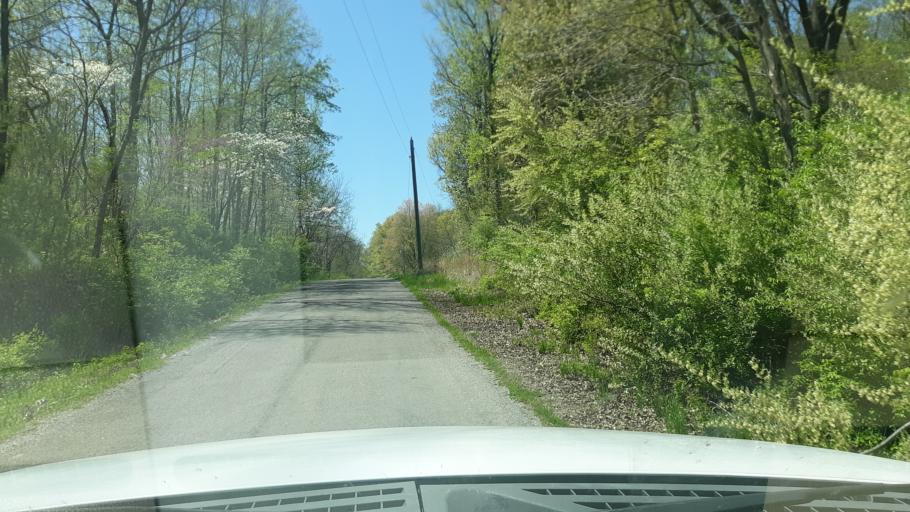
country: US
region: Illinois
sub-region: Saline County
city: Harrisburg
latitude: 37.8595
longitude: -88.6234
